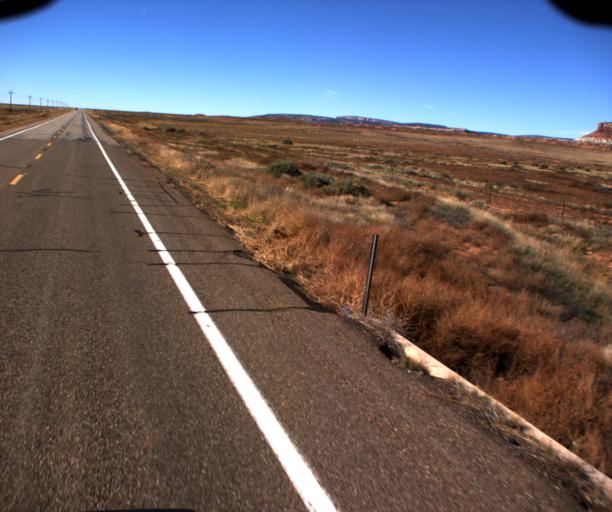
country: US
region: Arizona
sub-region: Coconino County
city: Fredonia
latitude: 36.8947
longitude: -112.6121
